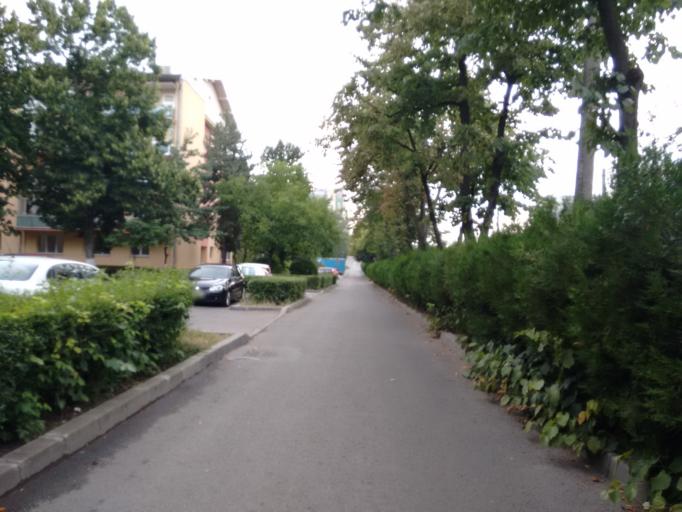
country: RO
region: Cluj
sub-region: Municipiul Cluj-Napoca
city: Cluj-Napoca
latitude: 46.7677
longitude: 23.6267
